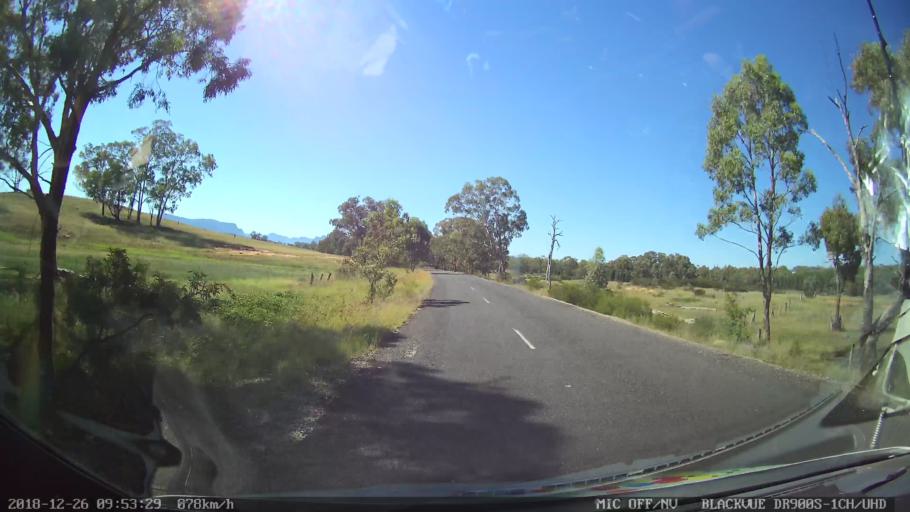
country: AU
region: New South Wales
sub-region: Mid-Western Regional
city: Kandos
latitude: -33.0213
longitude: 150.1536
